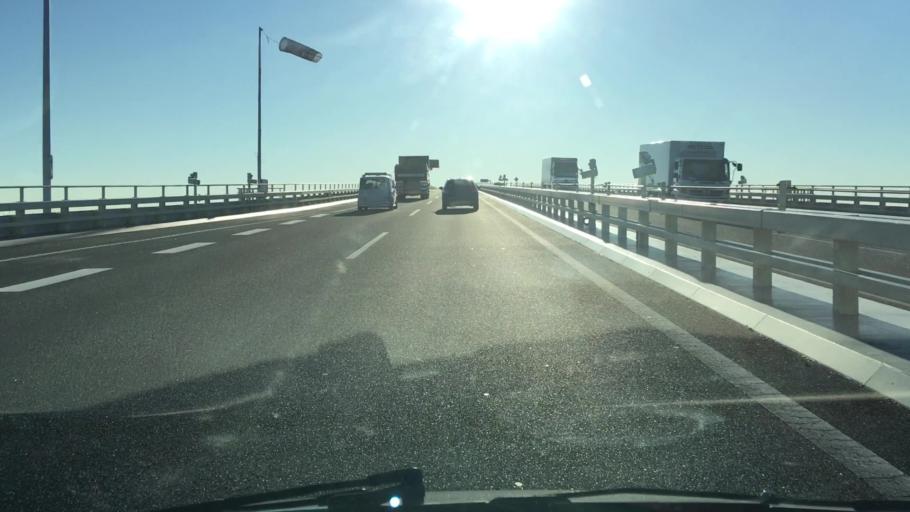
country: JP
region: Chiba
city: Kisarazu
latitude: 35.4593
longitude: 139.8820
